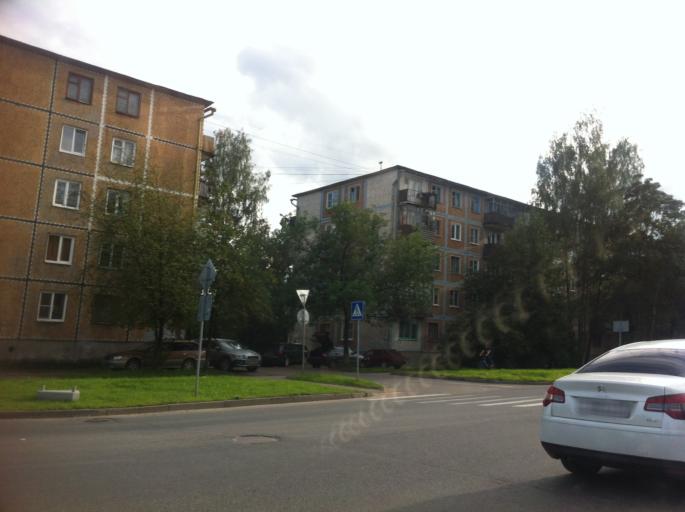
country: RU
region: Pskov
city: Pskov
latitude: 57.8215
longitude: 28.3201
